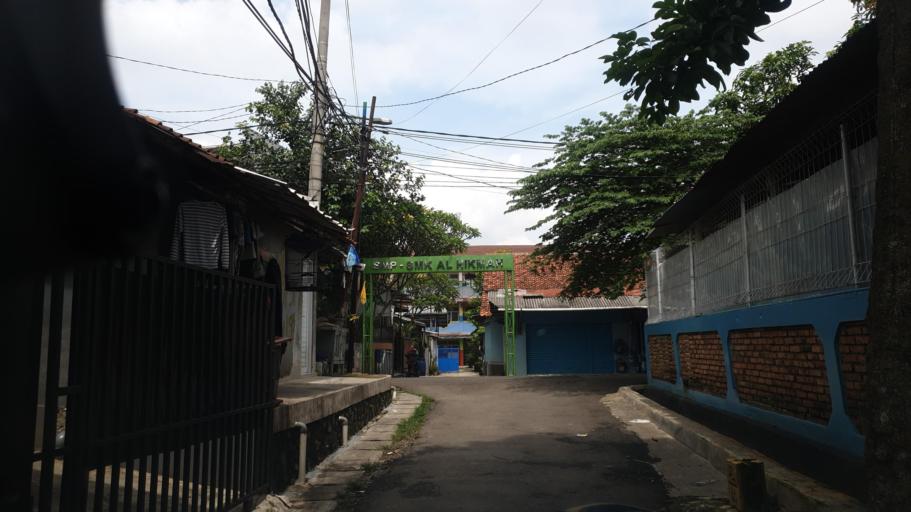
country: ID
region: West Java
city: Pamulang
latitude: -6.3370
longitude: 106.7700
